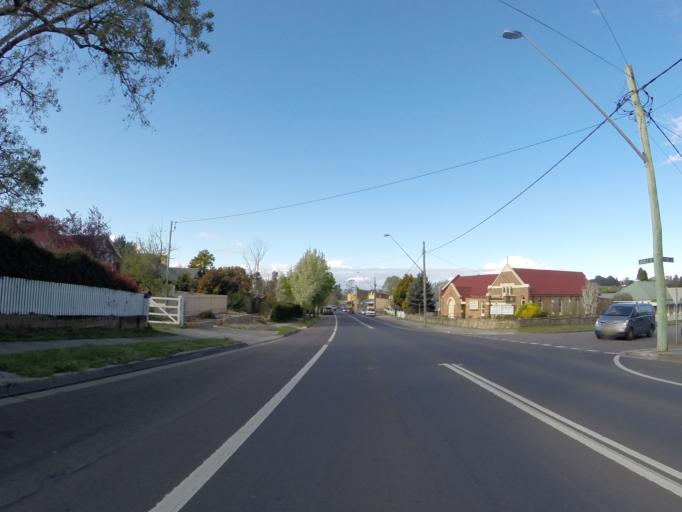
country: AU
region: New South Wales
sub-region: Wingecarribee
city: Moss Vale
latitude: -34.5530
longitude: 150.3652
